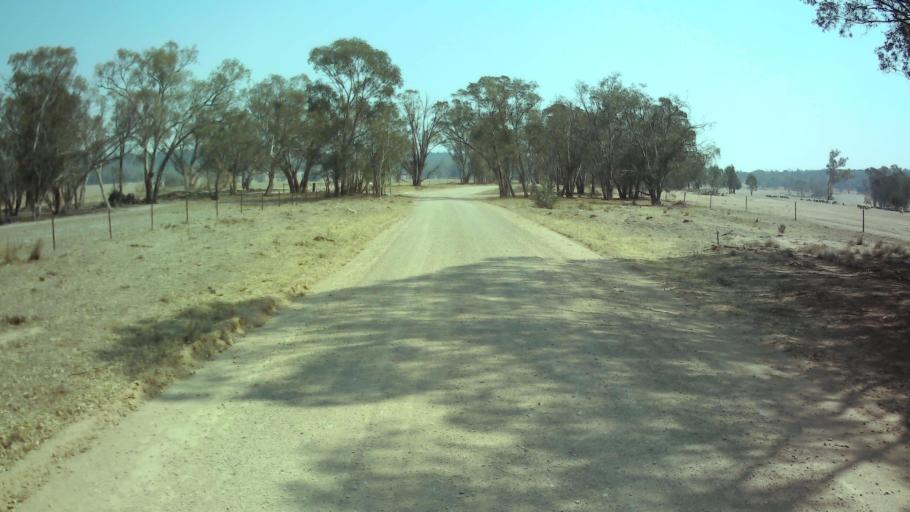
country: AU
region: New South Wales
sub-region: Weddin
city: Grenfell
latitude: -33.6735
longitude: 148.2752
